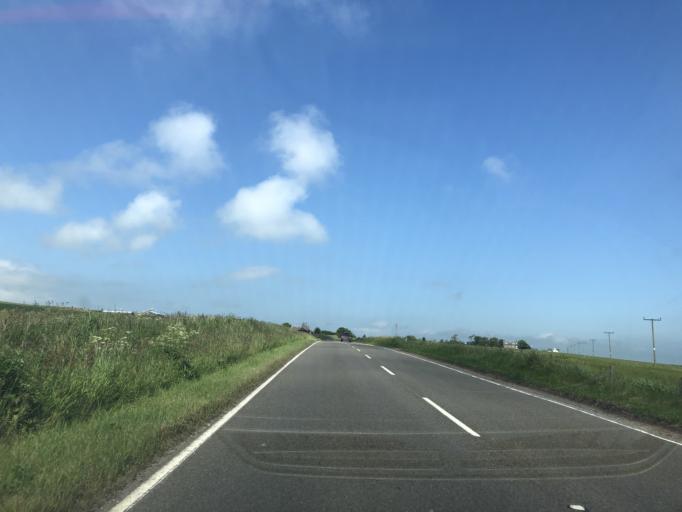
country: GB
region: Scotland
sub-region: Aberdeenshire
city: Stonehaven
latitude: 56.9285
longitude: -2.2067
